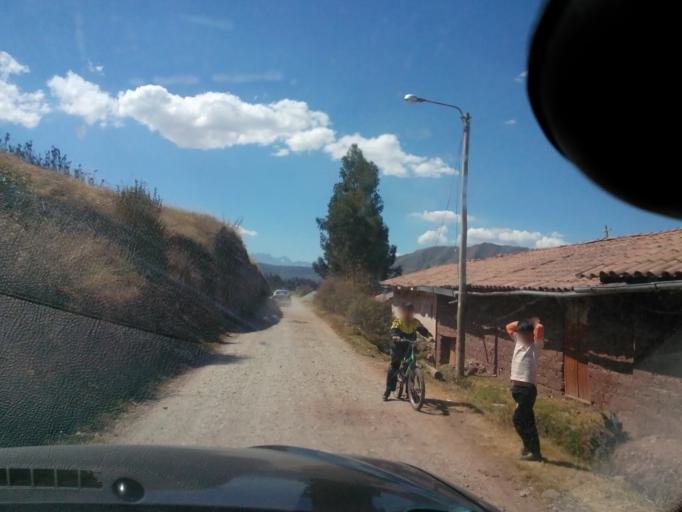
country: PE
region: Cusco
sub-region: Provincia de Anta
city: Zurite
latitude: -13.4435
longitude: -72.2399
